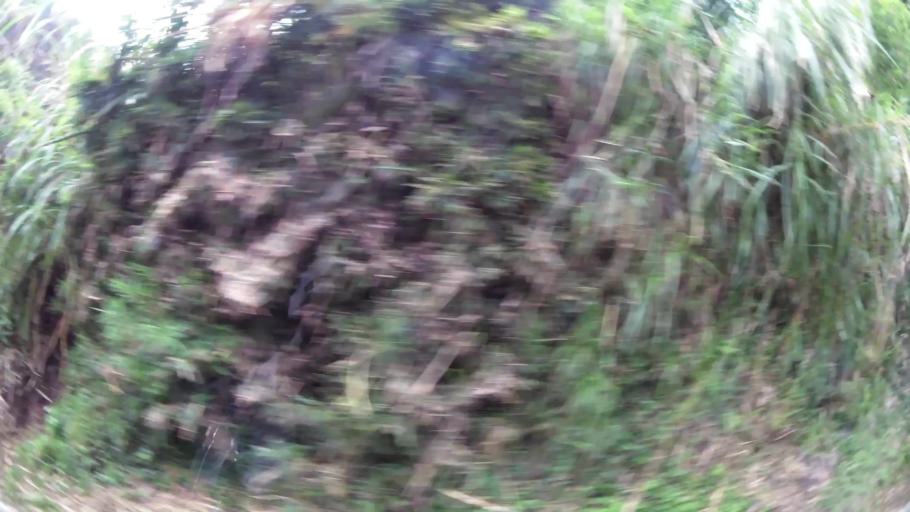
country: CO
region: Antioquia
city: La Estrella
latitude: 6.1725
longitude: -75.6576
